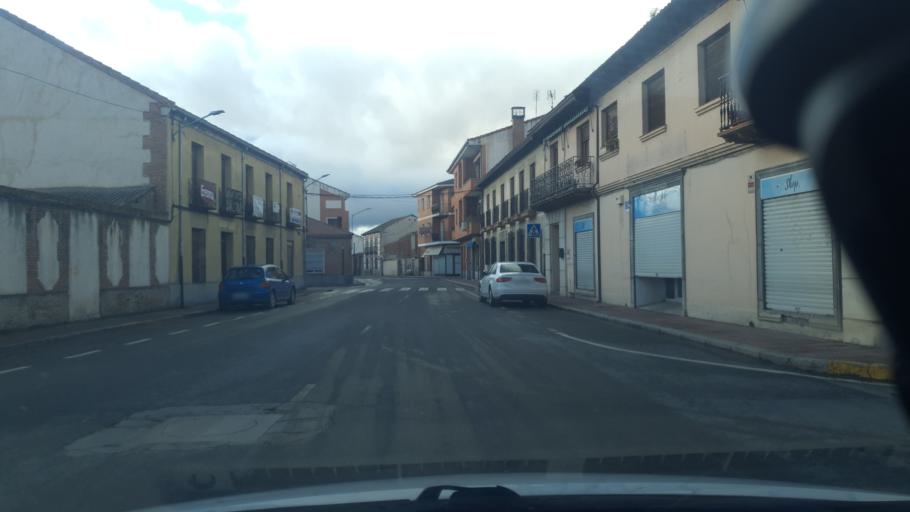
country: ES
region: Castille and Leon
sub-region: Provincia de Segovia
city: Nava de la Asuncion
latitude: 41.1569
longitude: -4.4876
